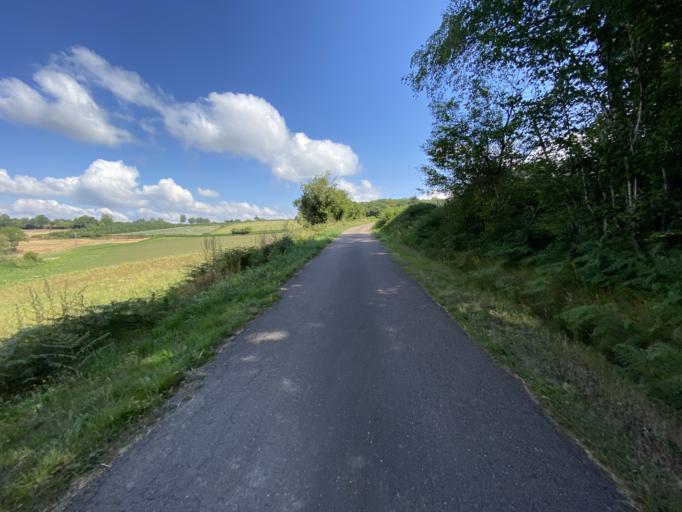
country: FR
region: Bourgogne
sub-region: Departement de la Cote-d'Or
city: Saulieu
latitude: 47.2726
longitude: 4.1560
